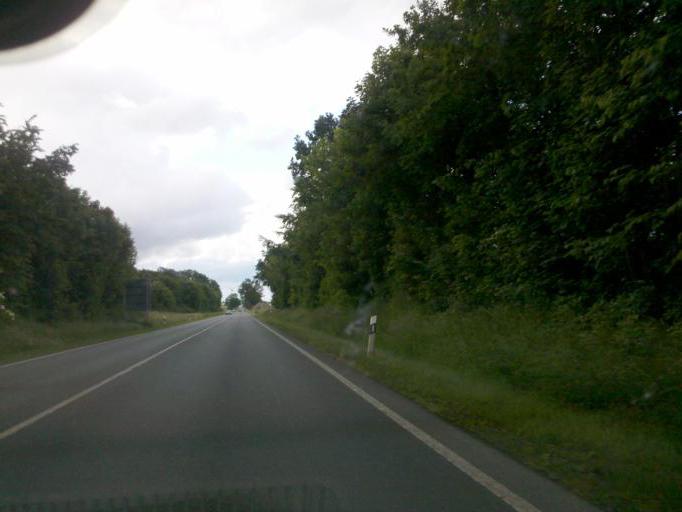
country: DE
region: North Rhine-Westphalia
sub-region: Regierungsbezirk Arnsberg
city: Anrochte
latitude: 51.5307
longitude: 8.3231
